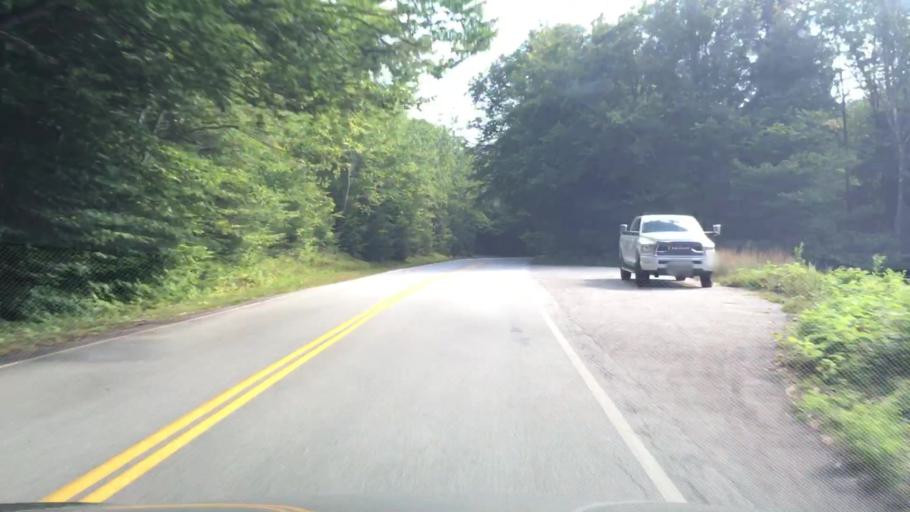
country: US
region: New Hampshire
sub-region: Carroll County
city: North Conway
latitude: 44.0478
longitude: -71.2763
